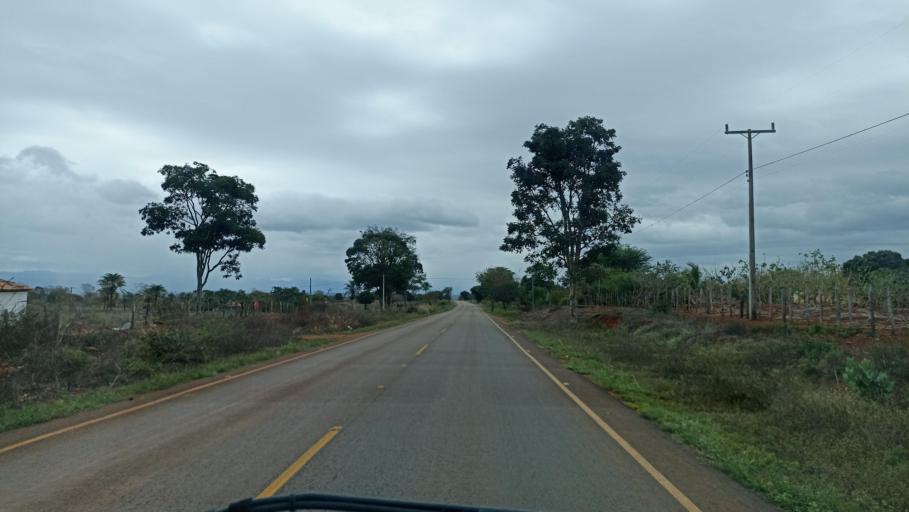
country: BR
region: Bahia
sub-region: Andarai
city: Vera Cruz
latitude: -12.9735
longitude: -41.0236
